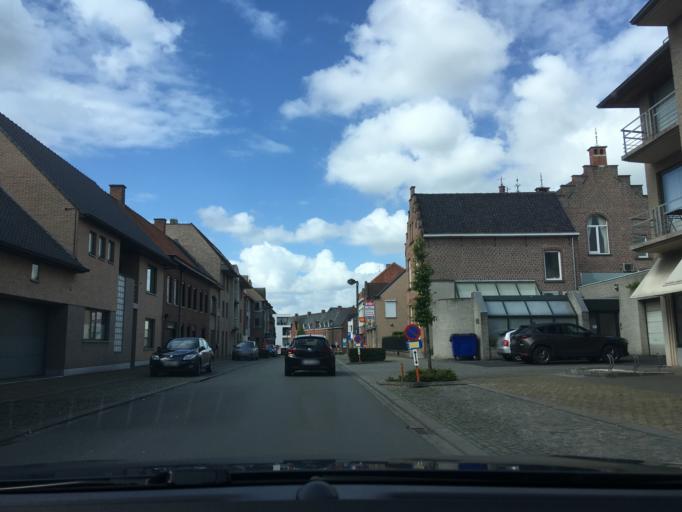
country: BE
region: Flanders
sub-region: Provincie West-Vlaanderen
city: Pittem
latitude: 50.9930
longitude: 3.2651
